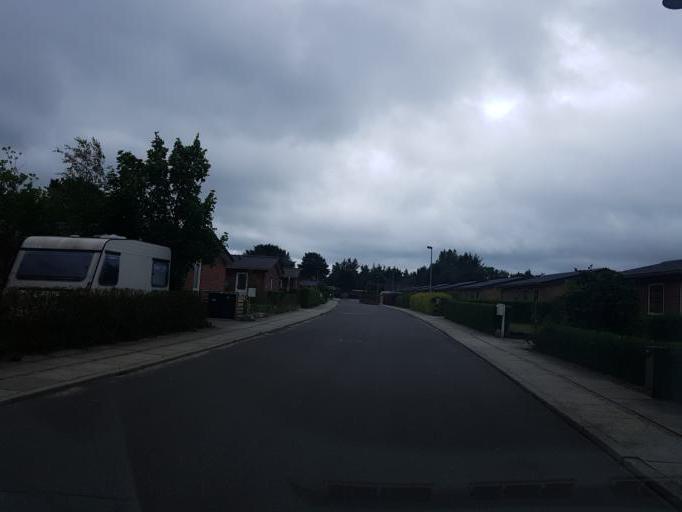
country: DK
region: South Denmark
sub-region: Varde Kommune
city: Varde
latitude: 55.6099
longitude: 8.4678
